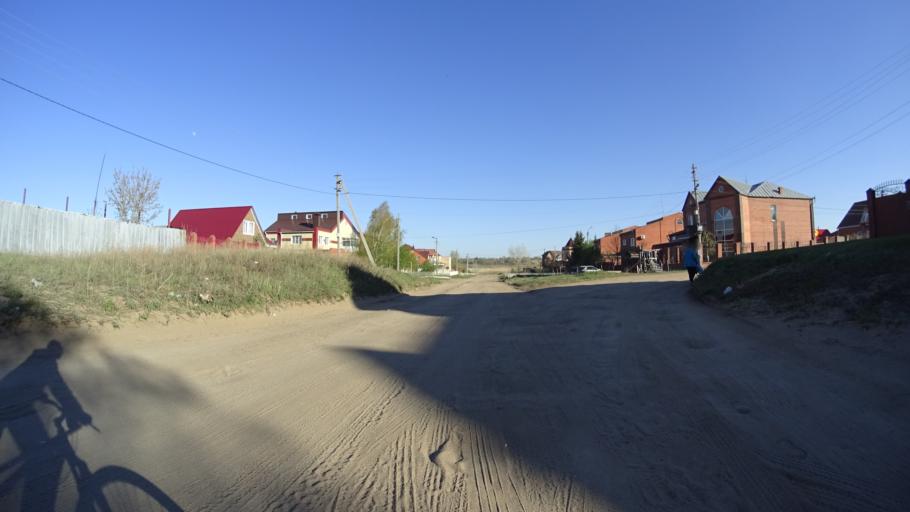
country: RU
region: Chelyabinsk
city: Troitsk
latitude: 54.0712
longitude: 61.5363
